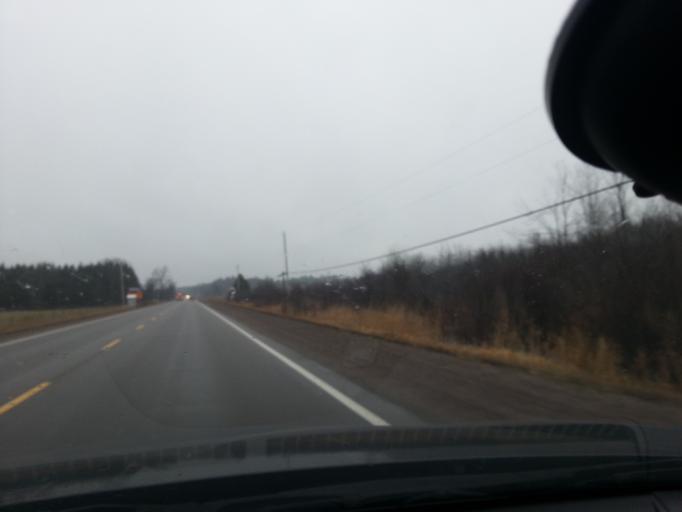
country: CA
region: Ontario
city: Belleville
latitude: 44.5571
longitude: -77.2731
